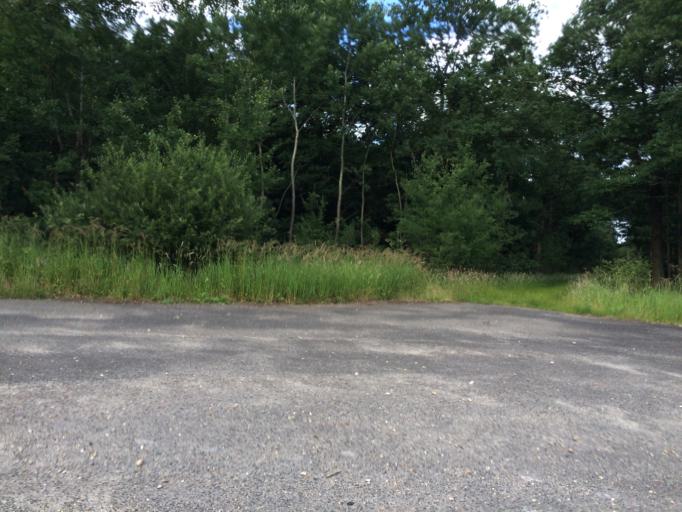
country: FR
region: Ile-de-France
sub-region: Departement de l'Essonne
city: Brunoy
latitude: 48.6671
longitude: 2.4854
